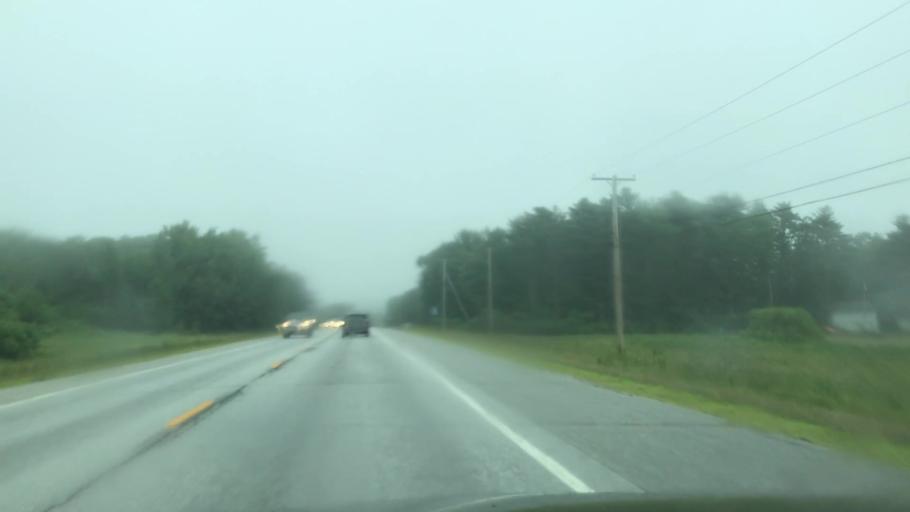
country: US
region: Maine
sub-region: Lincoln County
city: Nobleboro
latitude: 44.0877
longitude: -69.4713
